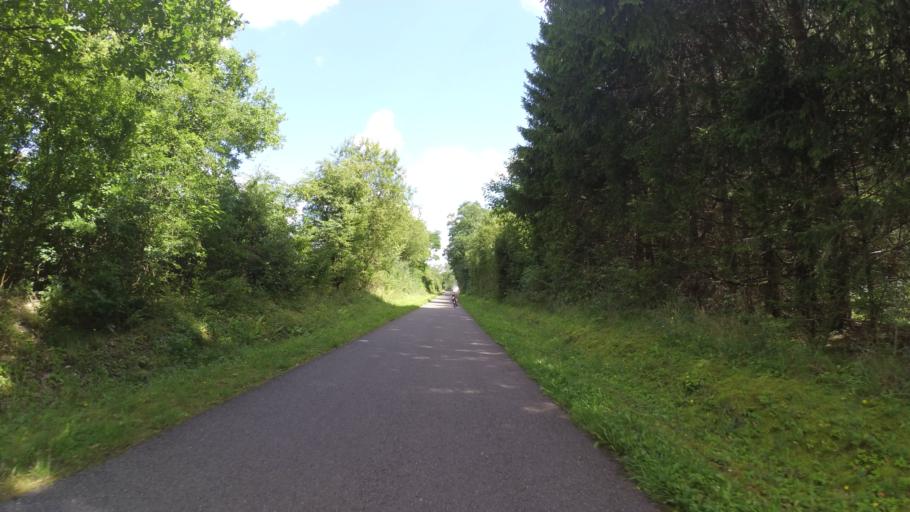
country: DE
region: Saarland
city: Oberthal
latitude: 49.5039
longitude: 7.0690
